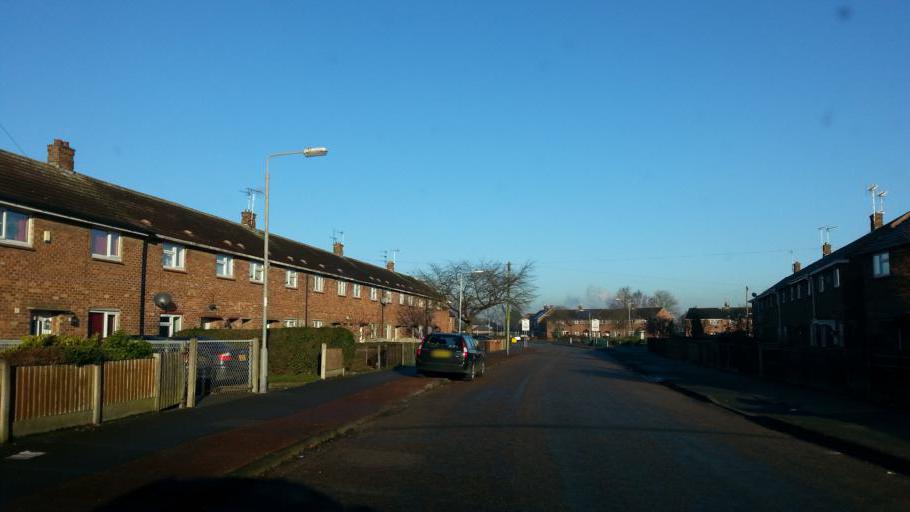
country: GB
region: England
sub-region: Nottinghamshire
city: Newark on Trent
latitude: 53.0602
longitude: -0.8117
